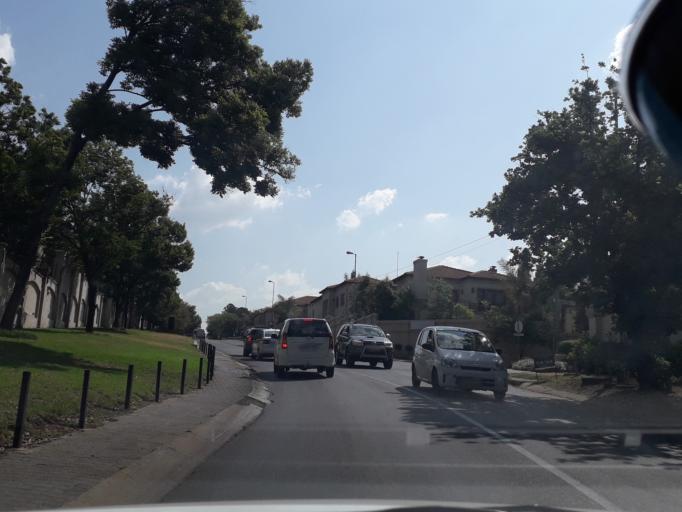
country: ZA
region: Gauteng
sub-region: City of Johannesburg Metropolitan Municipality
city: Modderfontein
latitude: -26.0836
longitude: 28.0531
